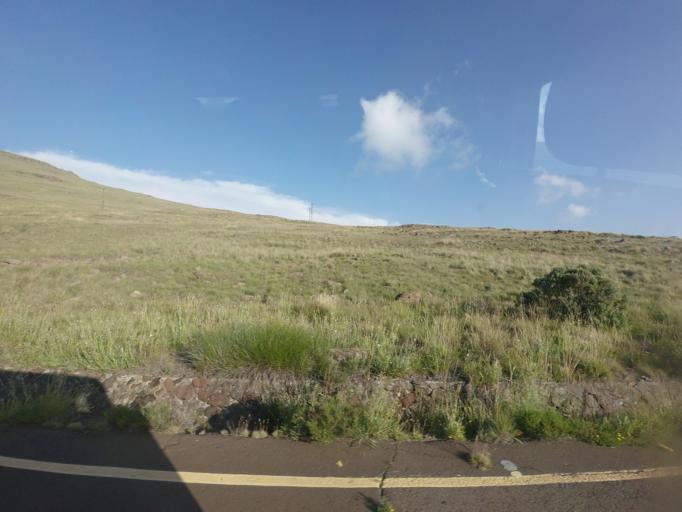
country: LS
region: Butha-Buthe
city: Butha-Buthe
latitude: -29.0959
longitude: 28.4233
